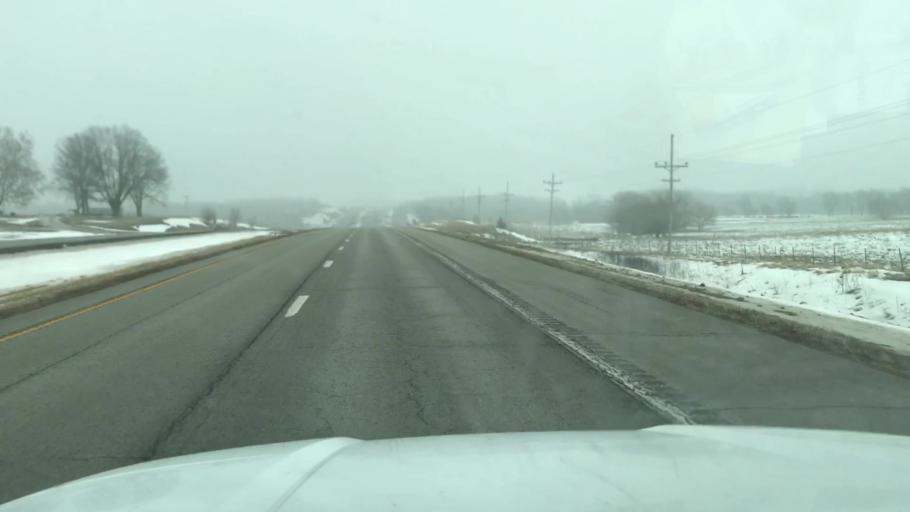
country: US
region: Missouri
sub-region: Clinton County
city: Cameron
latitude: 39.7545
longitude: -94.3270
